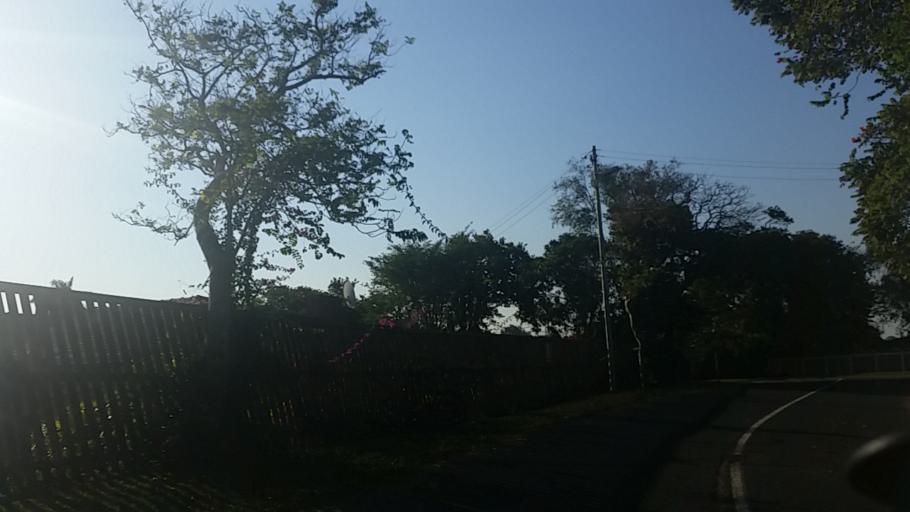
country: ZA
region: KwaZulu-Natal
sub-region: eThekwini Metropolitan Municipality
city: Berea
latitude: -29.8419
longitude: 30.9217
